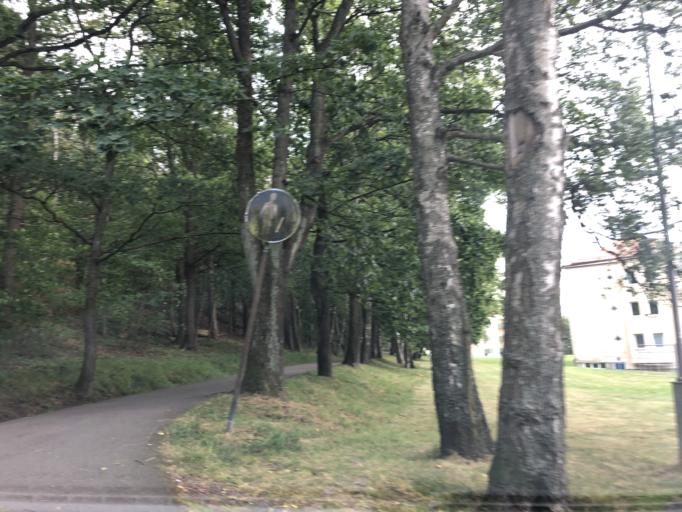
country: SE
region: Vaestra Goetaland
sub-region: Goteborg
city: Majorna
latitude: 57.7325
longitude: 11.9287
